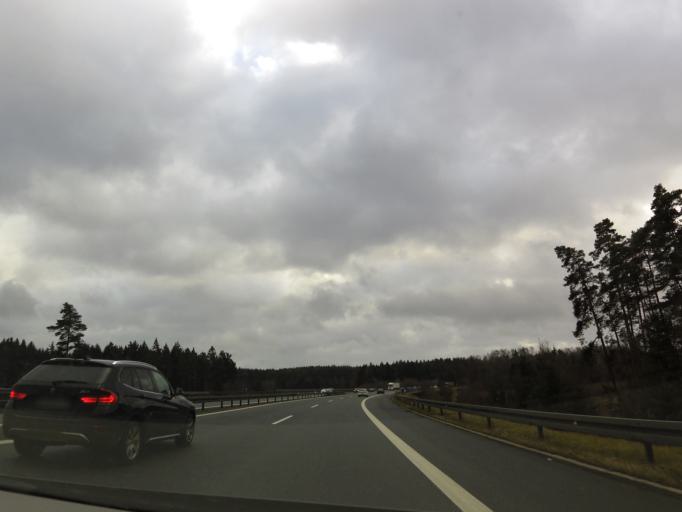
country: DE
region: Bavaria
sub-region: Upper Franconia
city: Schonwald
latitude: 50.2069
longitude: 12.1093
